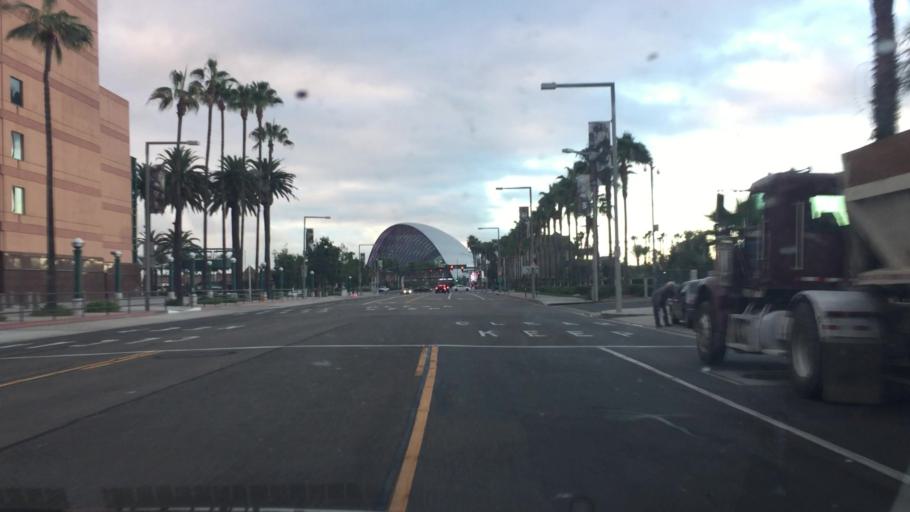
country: US
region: California
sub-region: Orange County
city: Orange
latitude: 33.8083
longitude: -117.8777
